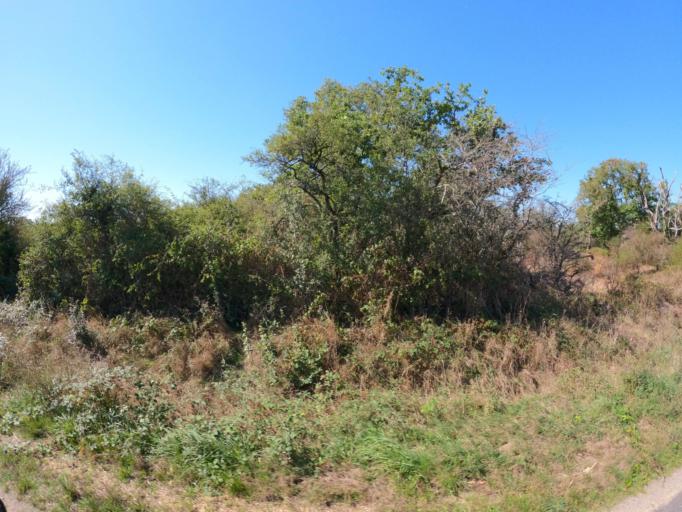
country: FR
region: Poitou-Charentes
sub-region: Departement de la Vienne
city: Lathus-Saint-Remy
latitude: 46.3164
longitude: 0.9756
